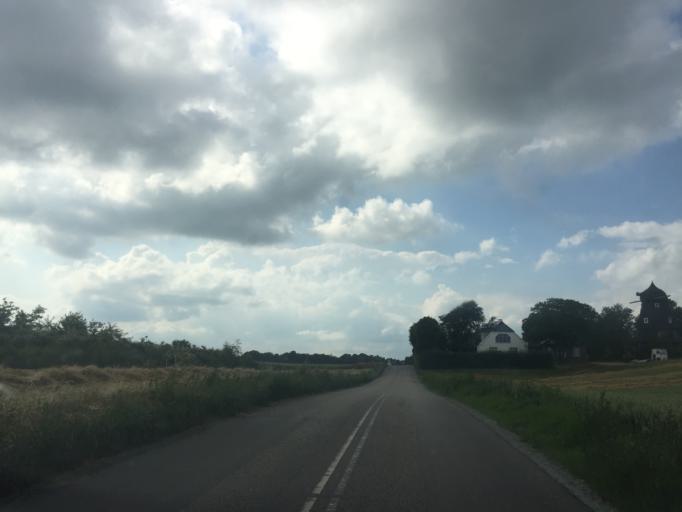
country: DK
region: Capital Region
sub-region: Hoje-Taastrup Kommune
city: Flong
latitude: 55.6880
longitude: 12.1765
